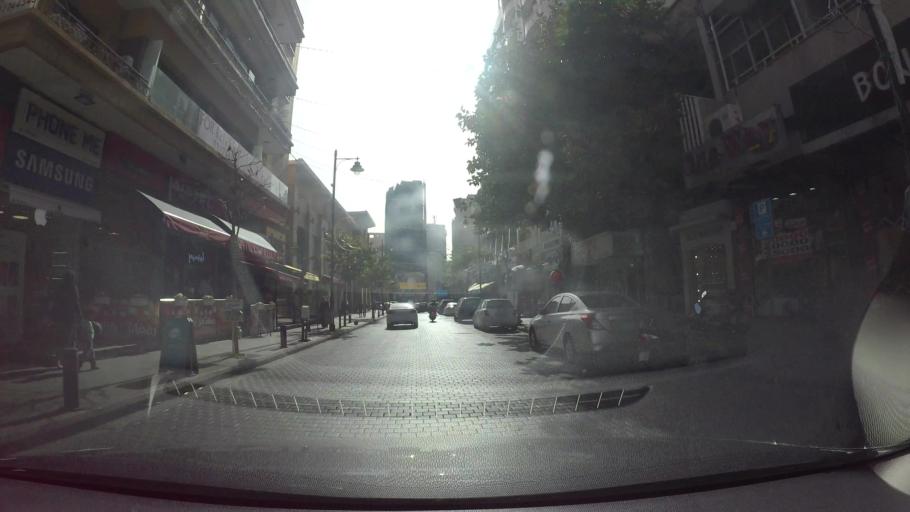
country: LB
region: Beyrouth
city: Ra's Bayrut
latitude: 33.8962
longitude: 35.4784
